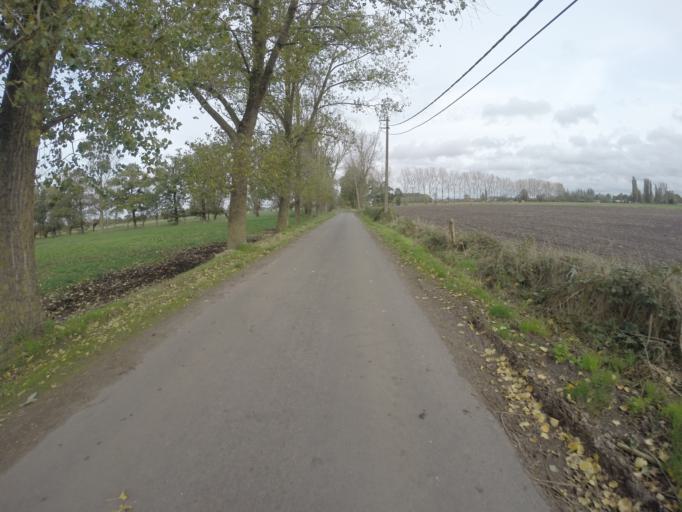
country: BE
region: Flanders
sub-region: Provincie Oost-Vlaanderen
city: Maldegem
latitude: 51.1827
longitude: 3.4294
